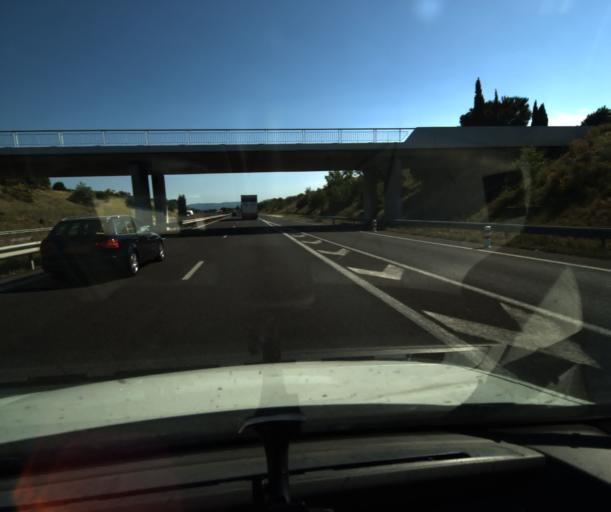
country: FR
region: Languedoc-Roussillon
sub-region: Departement des Pyrenees-Orientales
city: Villemolaque
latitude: 42.5805
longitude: 2.8452
